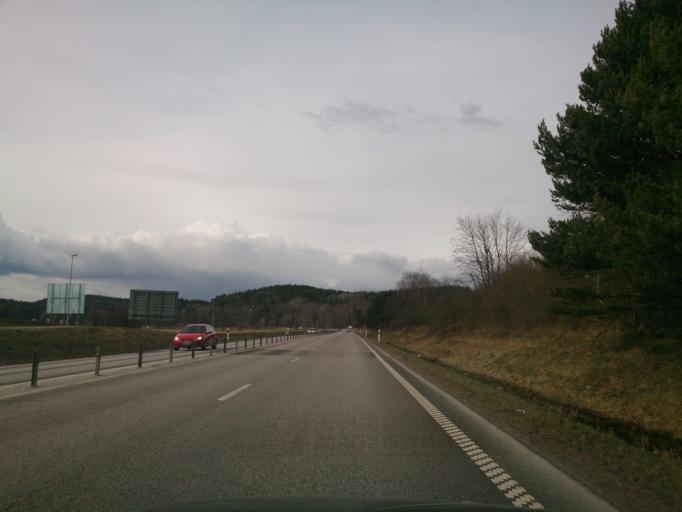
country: SE
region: OEstergoetland
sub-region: Norrkopings Kommun
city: Jursla
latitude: 58.6617
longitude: 16.1685
